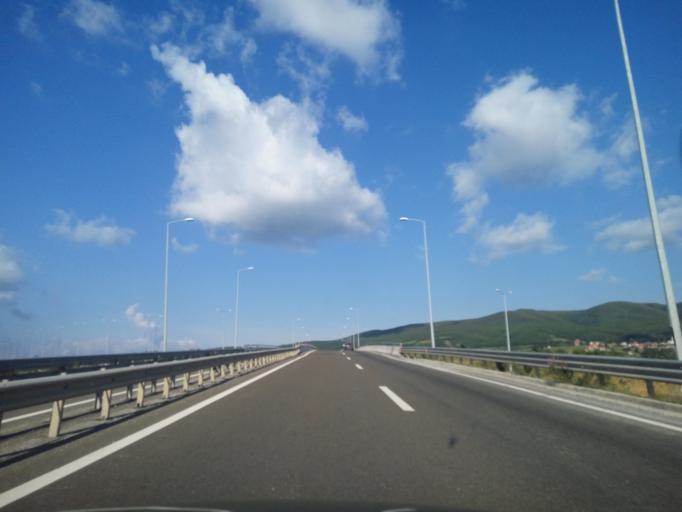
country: XK
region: Prizren
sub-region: Komuna e Malisheves
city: Llazice
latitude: 42.5512
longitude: 20.8123
